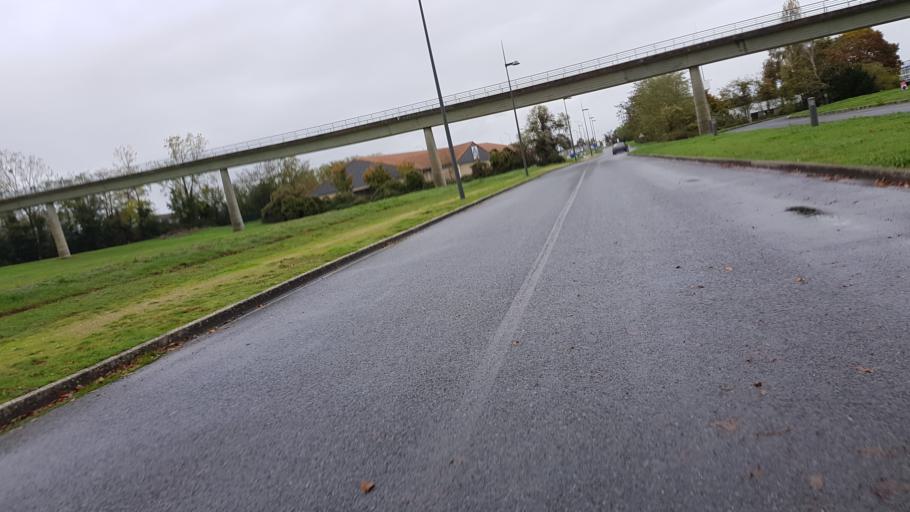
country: FR
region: Poitou-Charentes
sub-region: Departement de la Vienne
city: Jaunay-Clan
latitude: 46.6697
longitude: 0.3763
